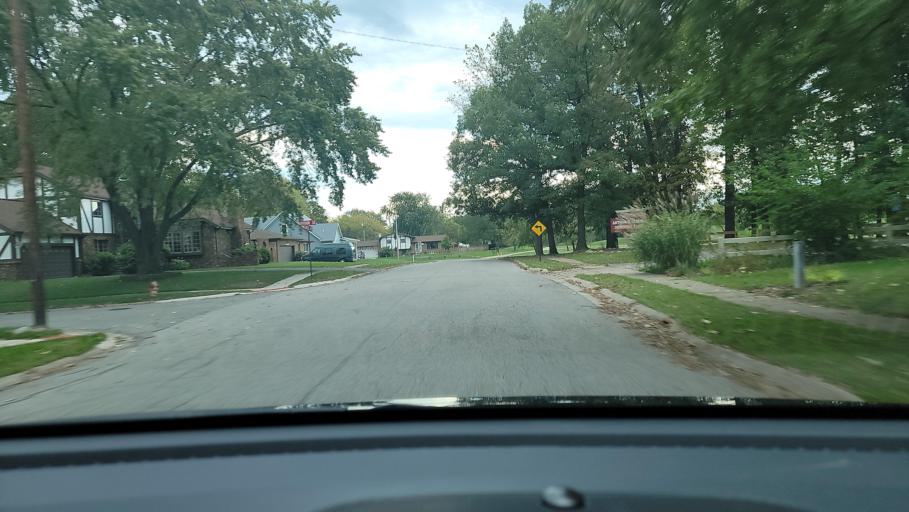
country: US
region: Indiana
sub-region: Porter County
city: Portage
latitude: 41.5686
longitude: -87.1765
